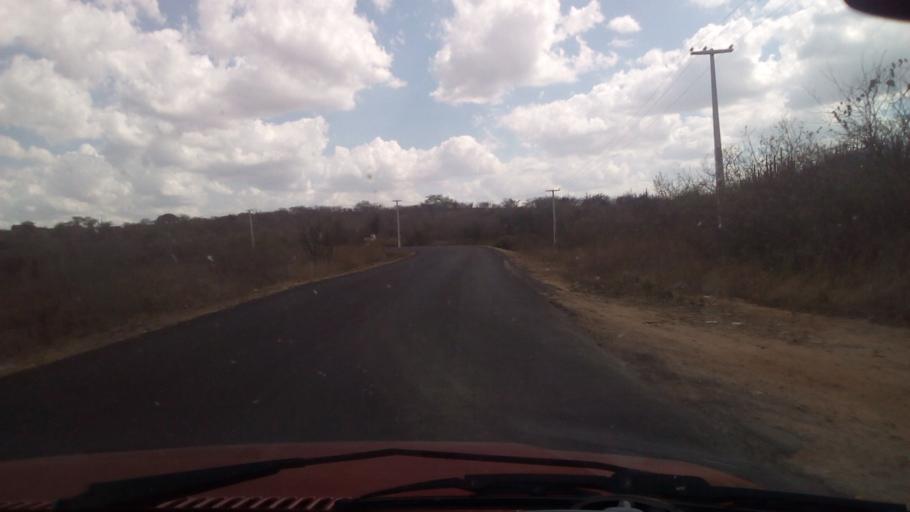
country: BR
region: Paraiba
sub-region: Cacimba De Dentro
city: Cacimba de Dentro
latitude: -6.6897
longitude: -35.7441
